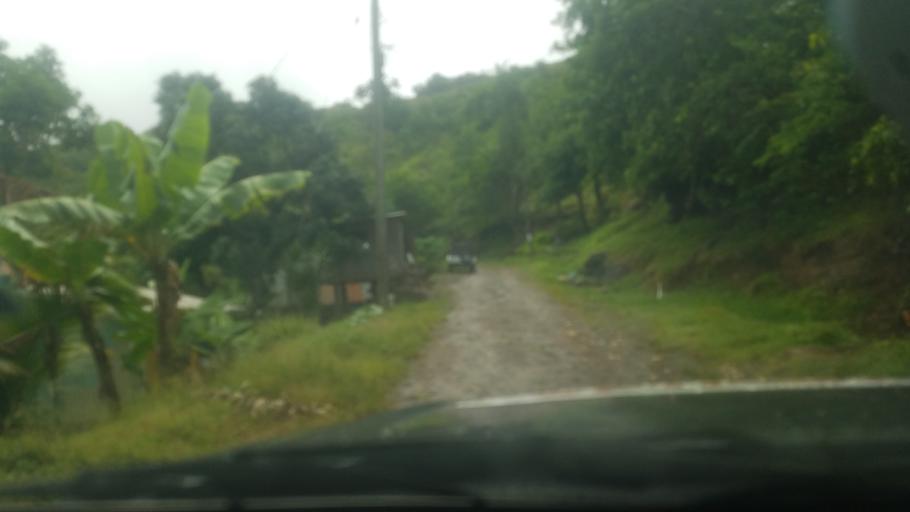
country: LC
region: Gros-Islet
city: Gros Islet
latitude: 14.0464
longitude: -60.9121
